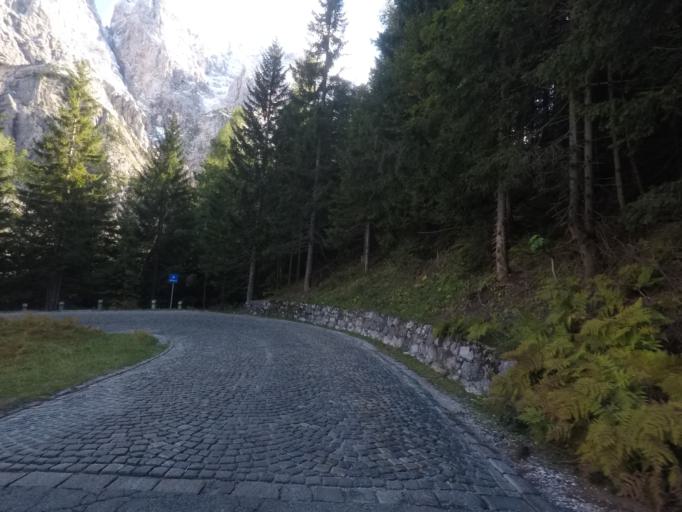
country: SI
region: Kranjska Gora
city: Kranjska Gora
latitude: 46.4392
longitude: 13.7598
